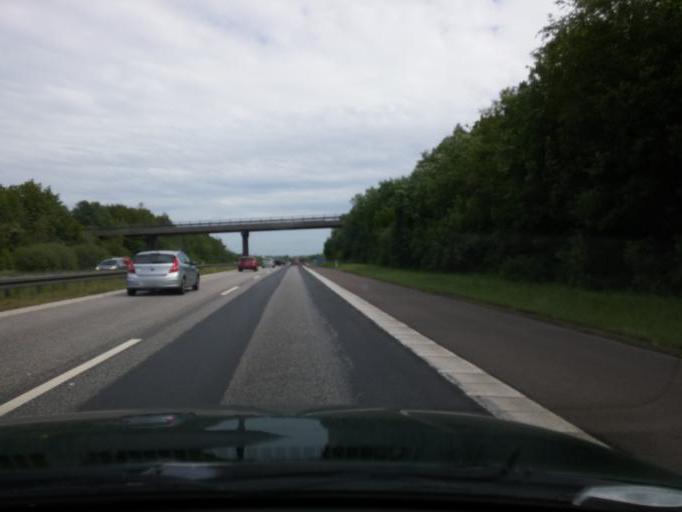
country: DK
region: South Denmark
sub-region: Assens Kommune
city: Vissenbjerg
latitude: 55.4054
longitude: 10.1398
